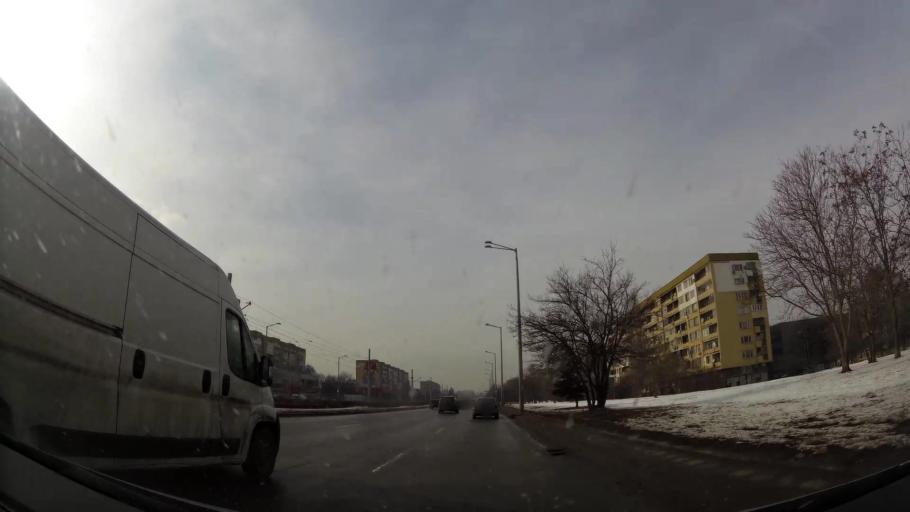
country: BG
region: Sofia-Capital
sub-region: Stolichna Obshtina
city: Sofia
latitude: 42.7004
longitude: 23.3706
